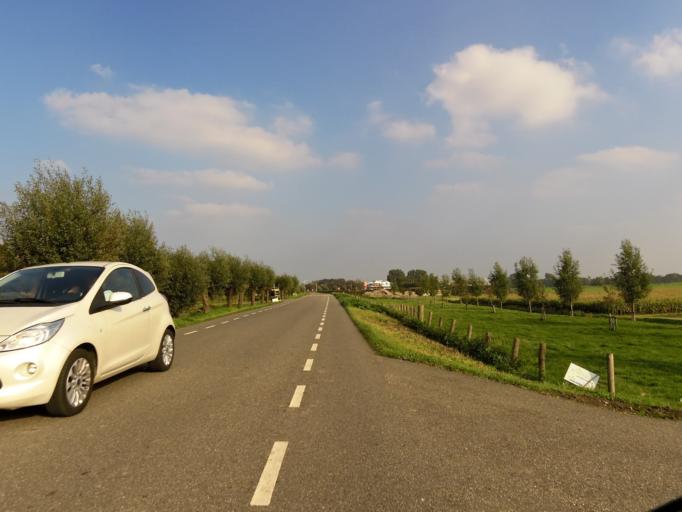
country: NL
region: South Holland
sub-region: Gemeente Rijnwoude
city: Benthuizen
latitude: 52.1043
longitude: 4.5441
